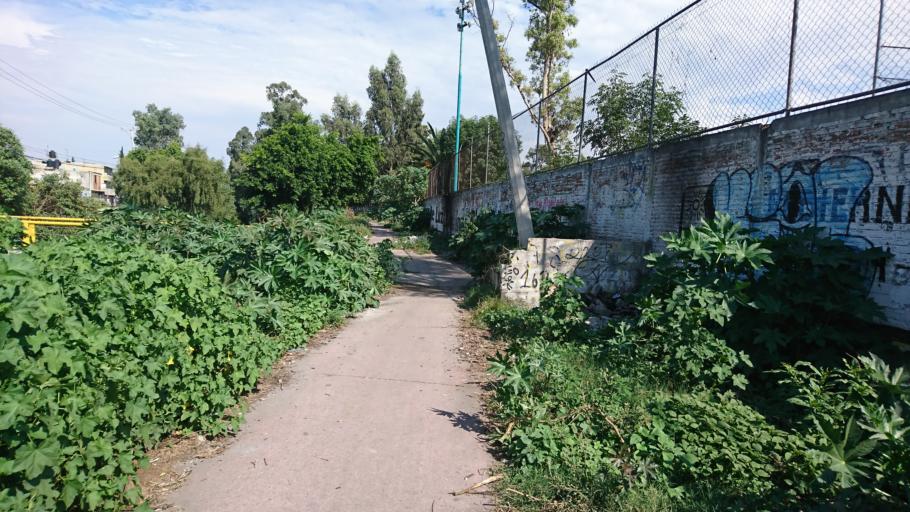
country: MX
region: Mexico City
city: Iztapalapa
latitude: 19.3342
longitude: -99.1123
